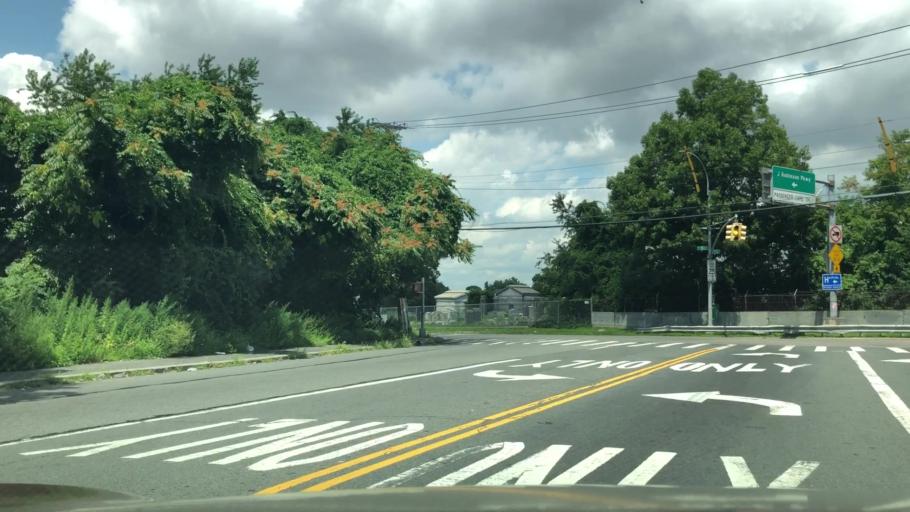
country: US
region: New York
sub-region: Kings County
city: East New York
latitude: 40.6911
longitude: -73.8906
